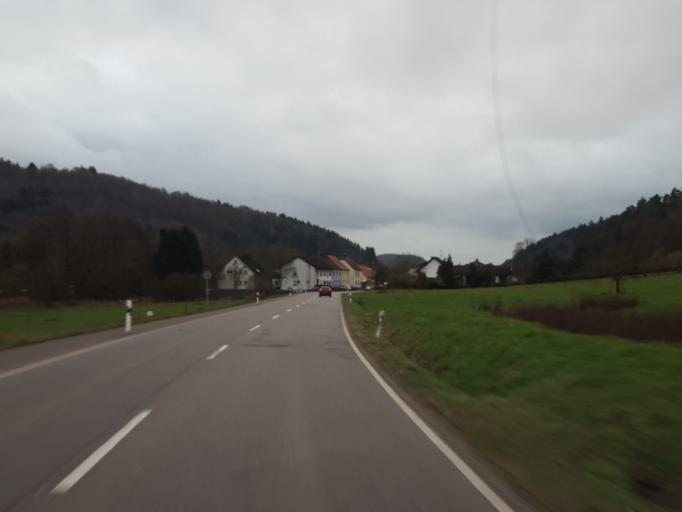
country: DE
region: Saarland
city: Beckingen
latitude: 49.4355
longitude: 6.7362
